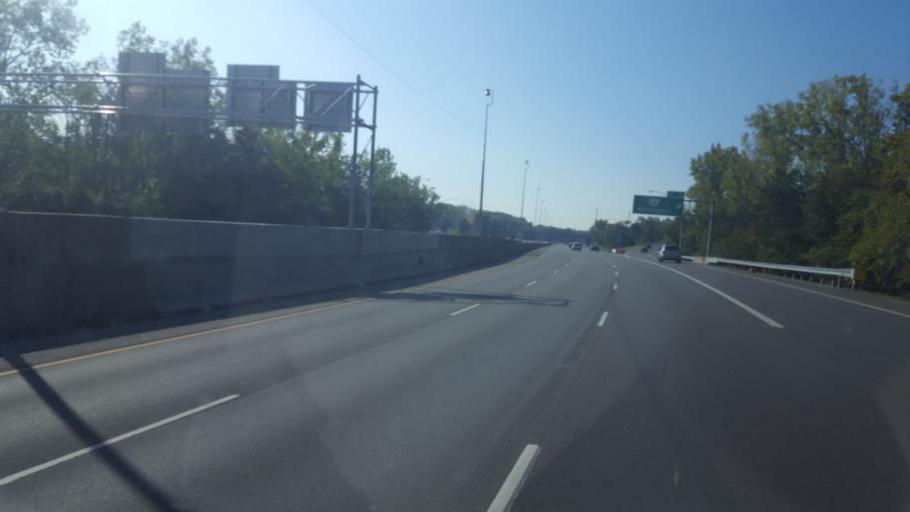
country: US
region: Ohio
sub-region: Franklin County
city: Worthington
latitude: 40.0930
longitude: -83.0374
